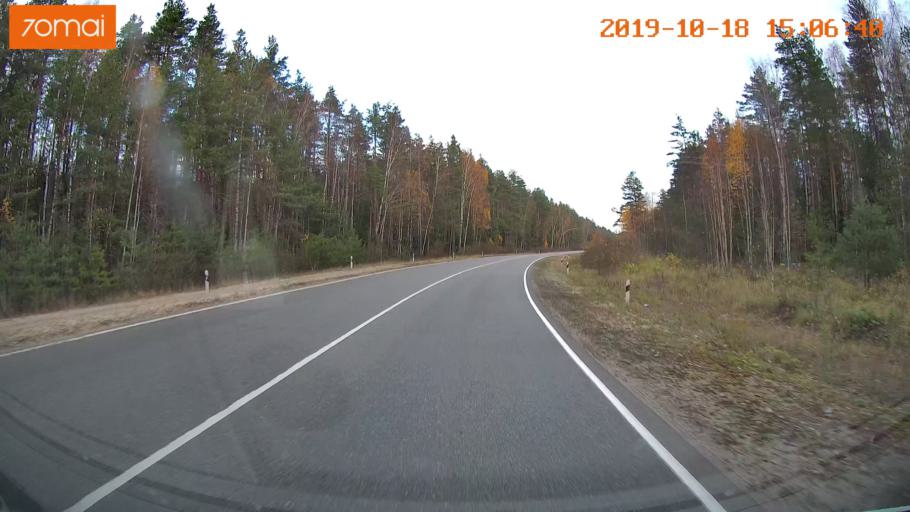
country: RU
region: Vladimir
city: Gus'-Khrustal'nyy
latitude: 55.5332
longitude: 40.5805
